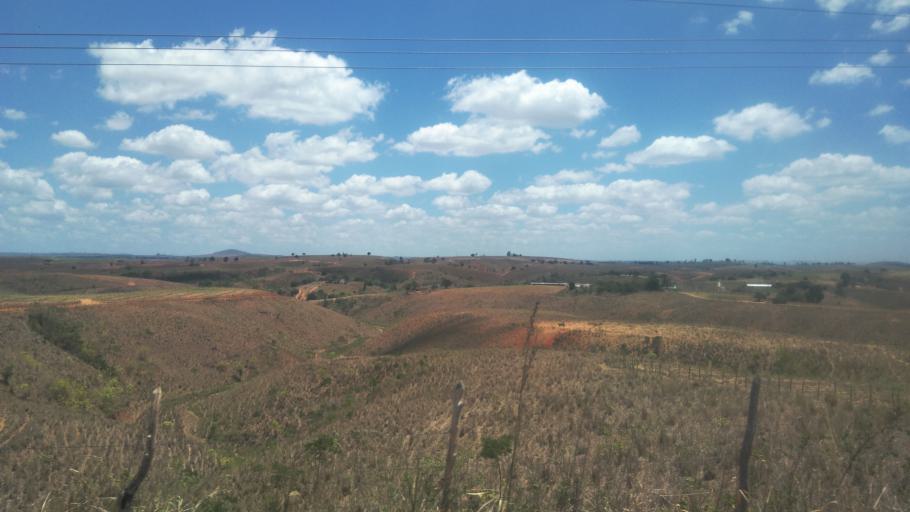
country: BR
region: Pernambuco
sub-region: Nazare Da Mata
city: Nazare da Mata
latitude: -7.7362
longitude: -35.2846
